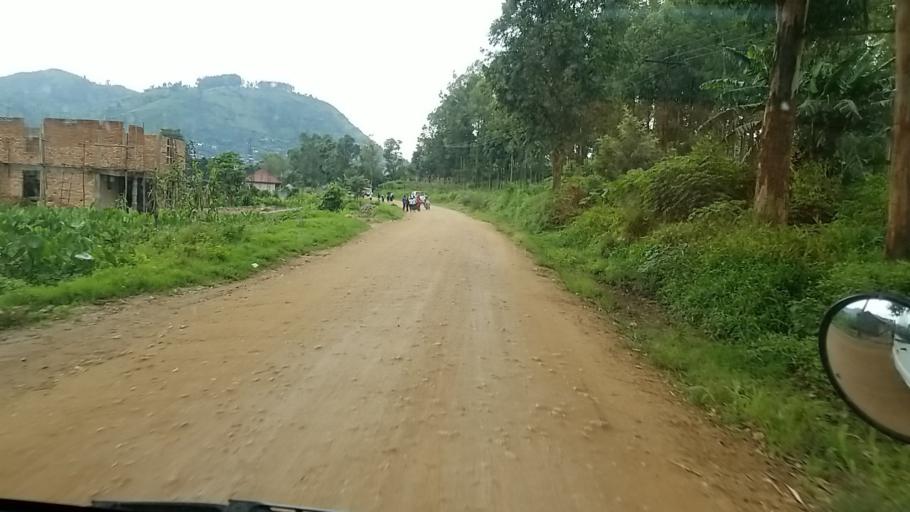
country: CD
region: Nord Kivu
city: Sake
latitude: -1.7022
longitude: 29.0157
